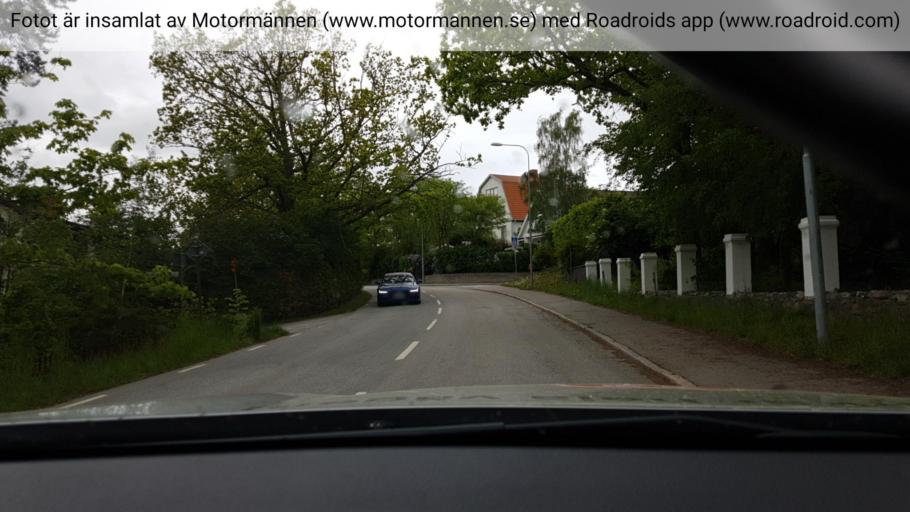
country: SE
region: Stockholm
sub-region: Lidingo
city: Brevik
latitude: 59.3474
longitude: 18.2170
